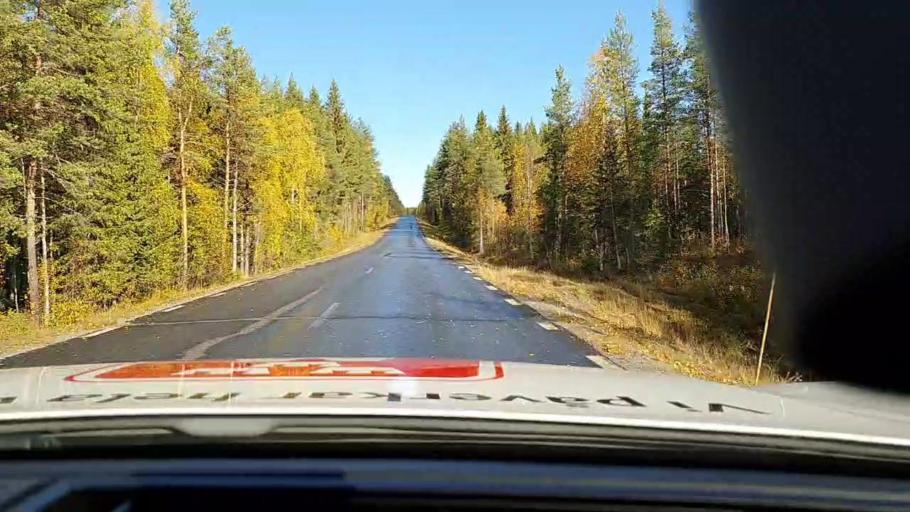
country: SE
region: Vaesterbotten
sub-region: Skelleftea Kommun
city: Langsele
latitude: 64.9541
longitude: 20.0336
